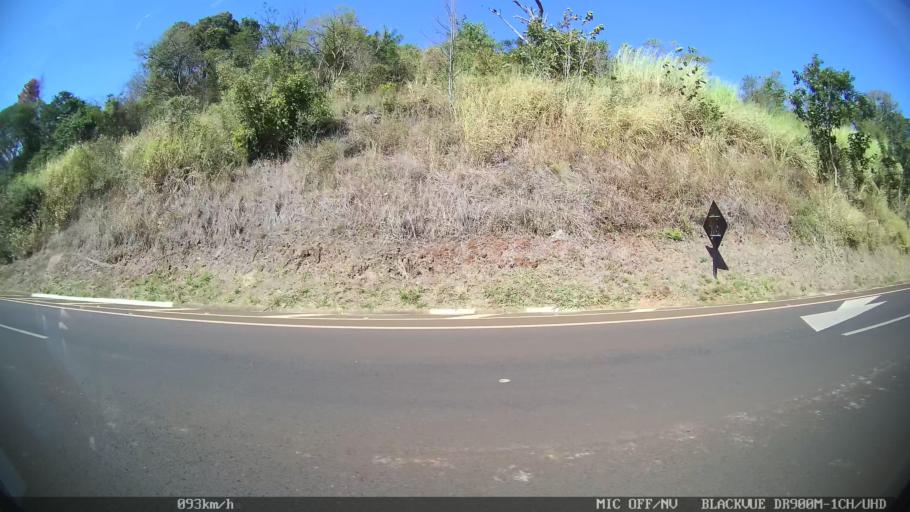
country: BR
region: Sao Paulo
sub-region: Franca
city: Franca
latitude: -20.6054
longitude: -47.4507
